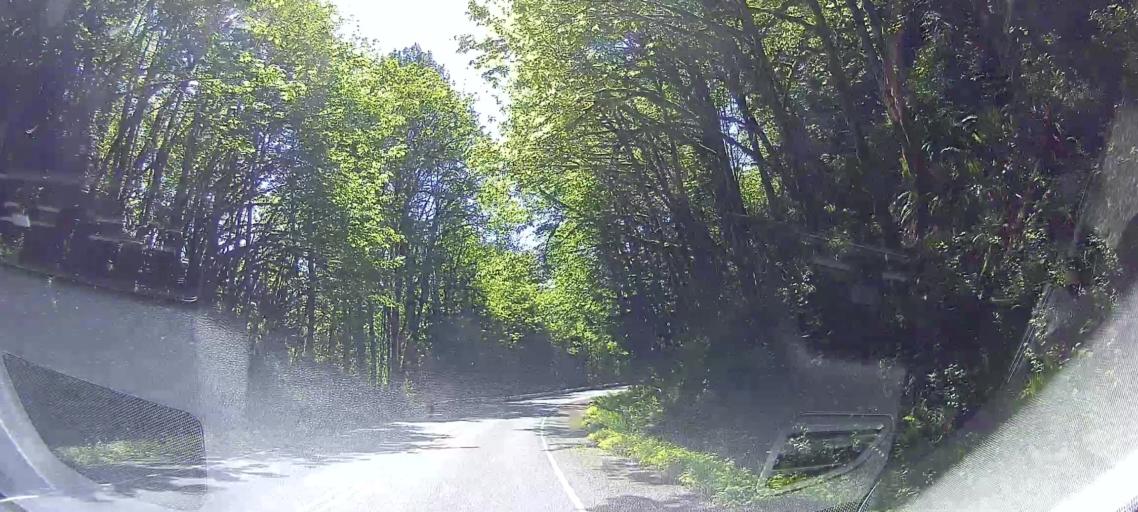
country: US
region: Washington
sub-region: Snohomish County
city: Darrington
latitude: 48.5184
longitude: -121.7257
